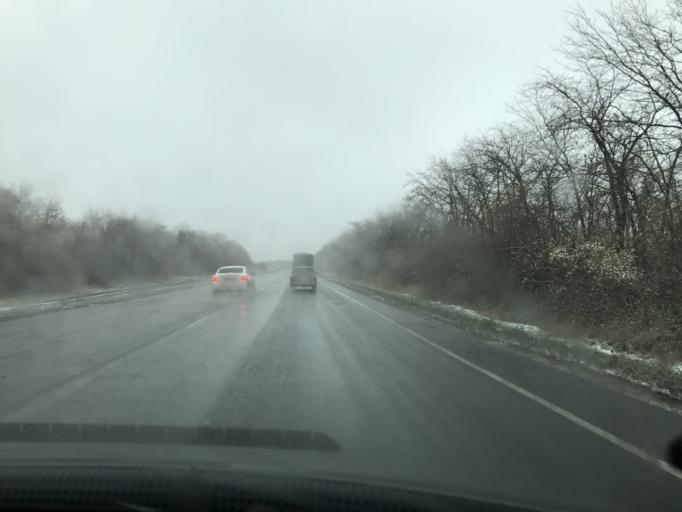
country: RU
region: Rostov
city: Kirovskaya
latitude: 46.9982
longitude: 39.9942
